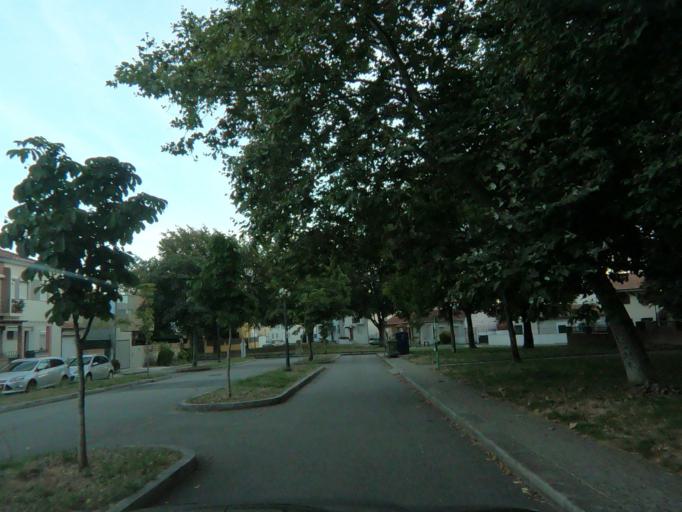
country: PT
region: Porto
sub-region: Porto
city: Porto
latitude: 41.1765
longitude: -8.6193
